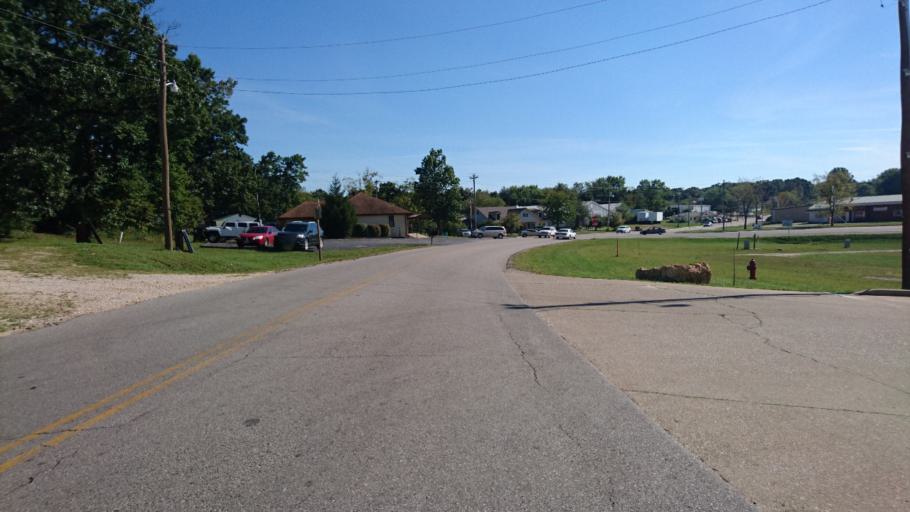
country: US
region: Missouri
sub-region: Crawford County
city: Bourbon
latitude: 38.1527
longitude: -91.2479
